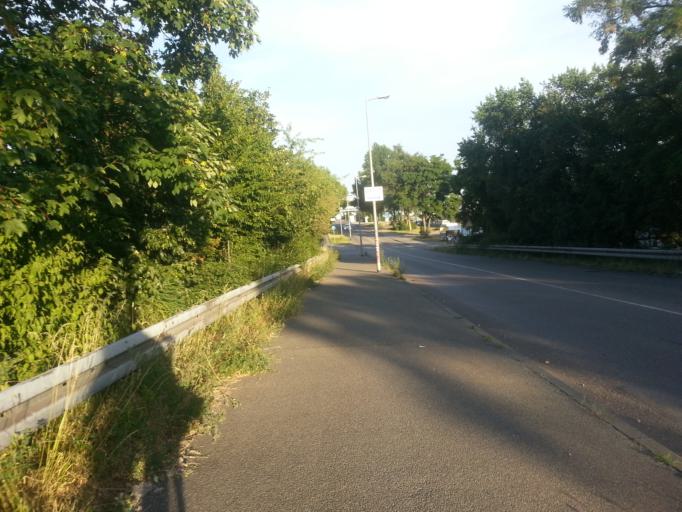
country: DE
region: Rheinland-Pfalz
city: Altrip
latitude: 49.4614
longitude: 8.4971
